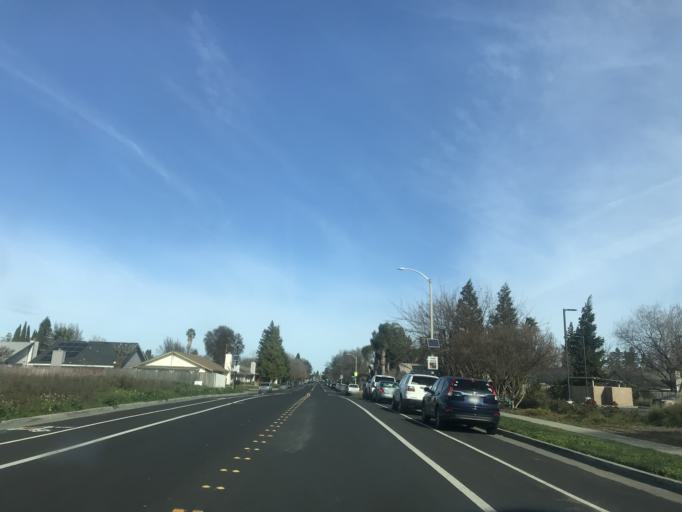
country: US
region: California
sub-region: Yolo County
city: Woodland
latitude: 38.6585
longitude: -121.7565
